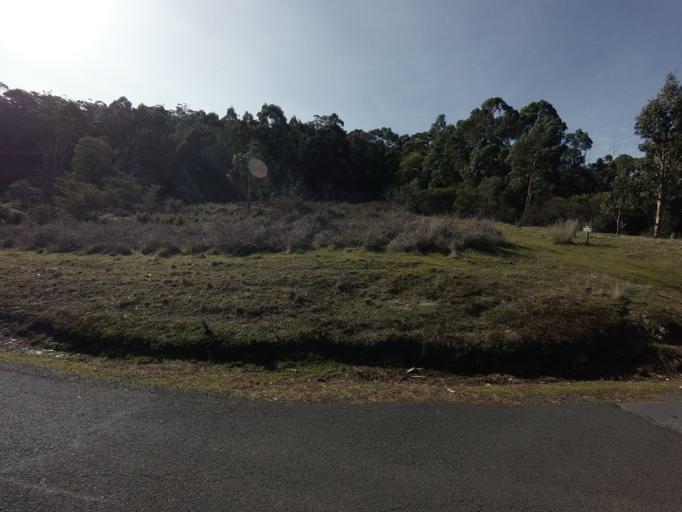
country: AU
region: Tasmania
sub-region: Kingborough
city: Kettering
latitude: -43.1200
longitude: 147.2577
